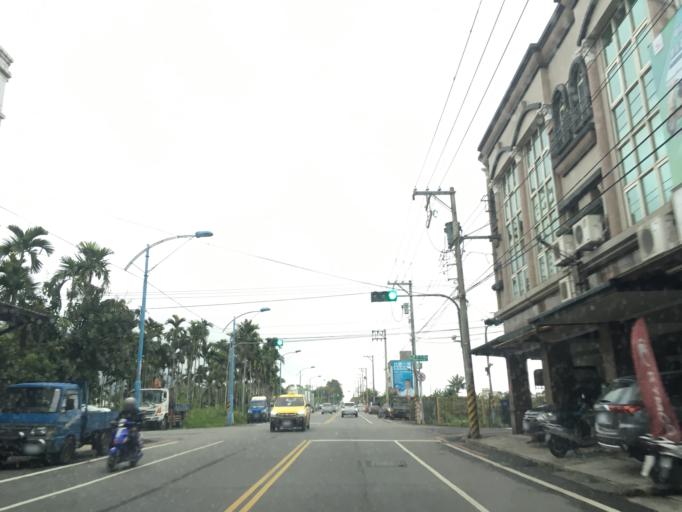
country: TW
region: Taiwan
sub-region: Hualien
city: Hualian
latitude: 23.9812
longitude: 121.5683
